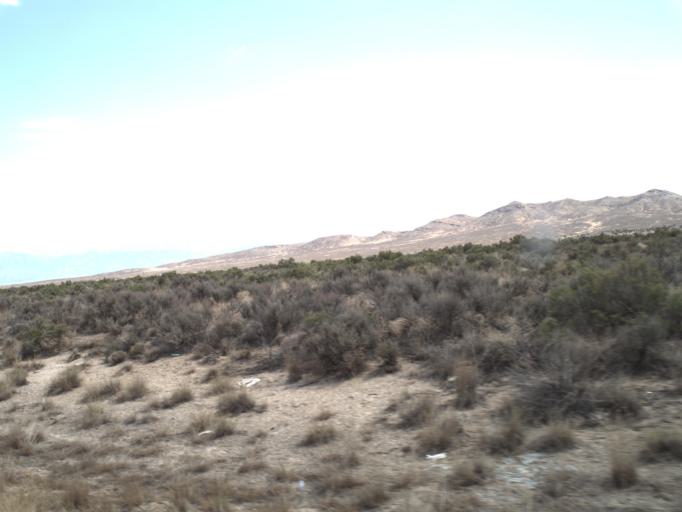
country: US
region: Utah
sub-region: Tooele County
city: Tooele
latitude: 40.1076
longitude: -112.4308
